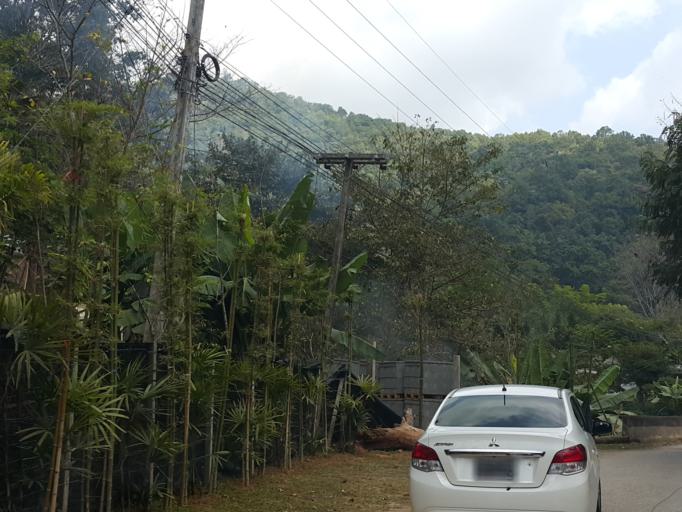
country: TH
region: Chiang Mai
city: Mae On
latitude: 18.8669
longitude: 99.3249
